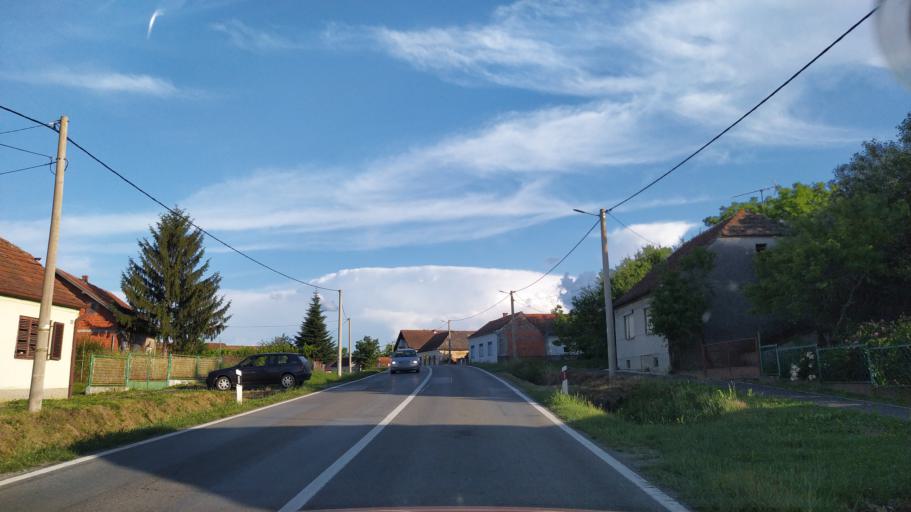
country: HR
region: Virovitick-Podravska
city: Slatina
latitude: 45.6675
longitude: 17.7628
